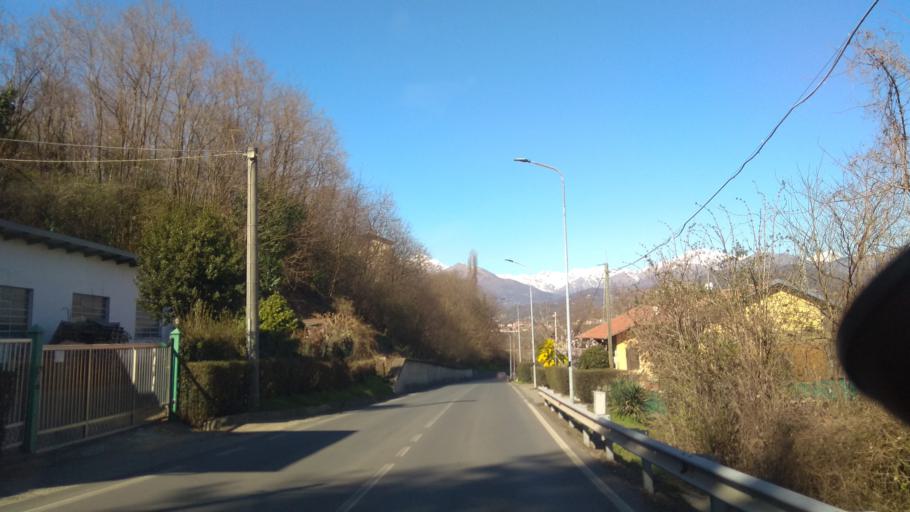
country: IT
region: Piedmont
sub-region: Provincia di Biella
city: Candelo
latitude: 45.5487
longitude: 8.1105
